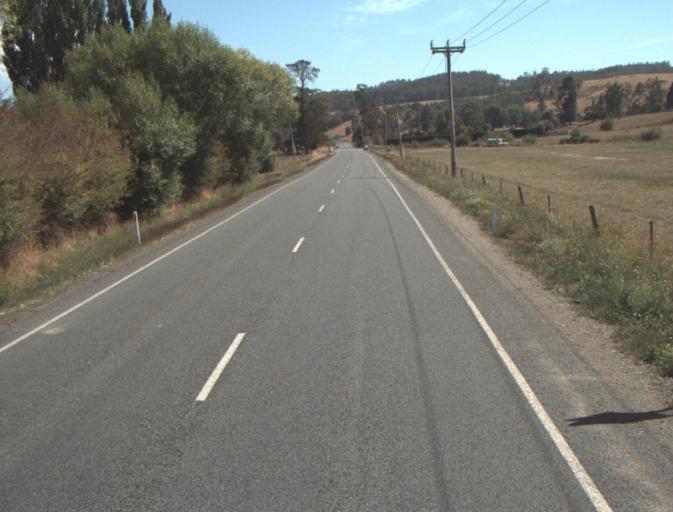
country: AU
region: Tasmania
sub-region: Launceston
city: Mayfield
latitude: -41.2476
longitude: 147.2176
